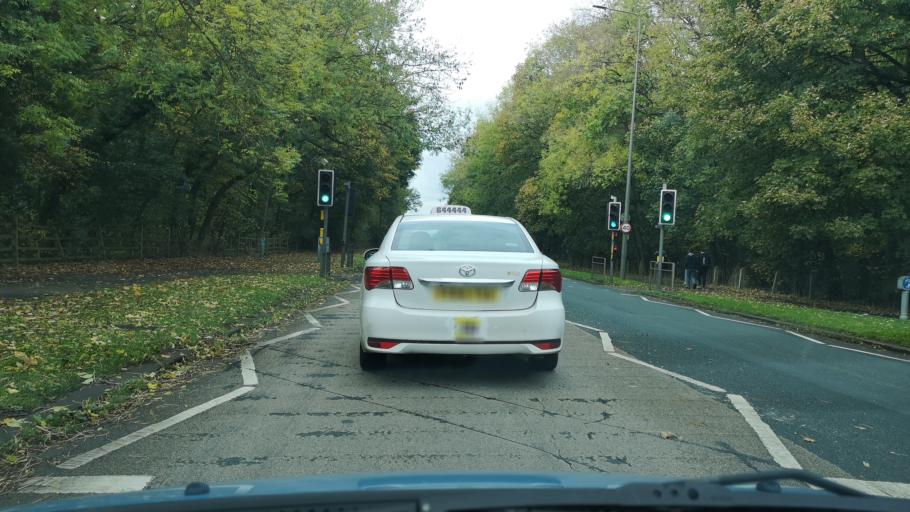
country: GB
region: England
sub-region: North Lincolnshire
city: Scunthorpe
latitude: 53.5824
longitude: -0.6705
